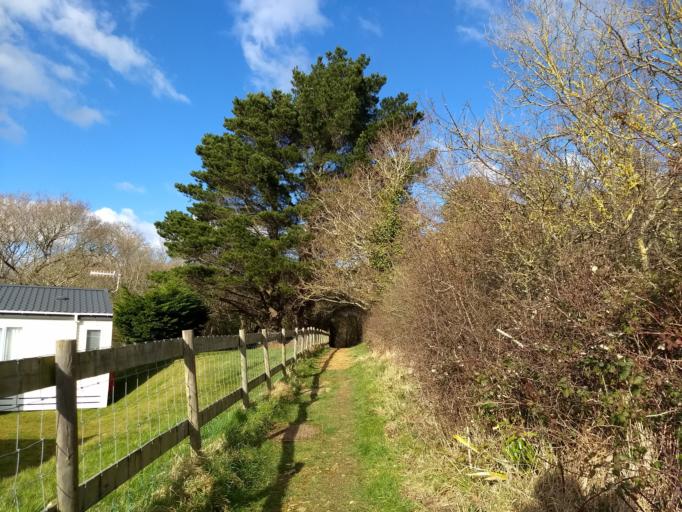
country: GB
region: England
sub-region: Isle of Wight
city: Bembridge
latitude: 50.6782
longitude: -1.0958
